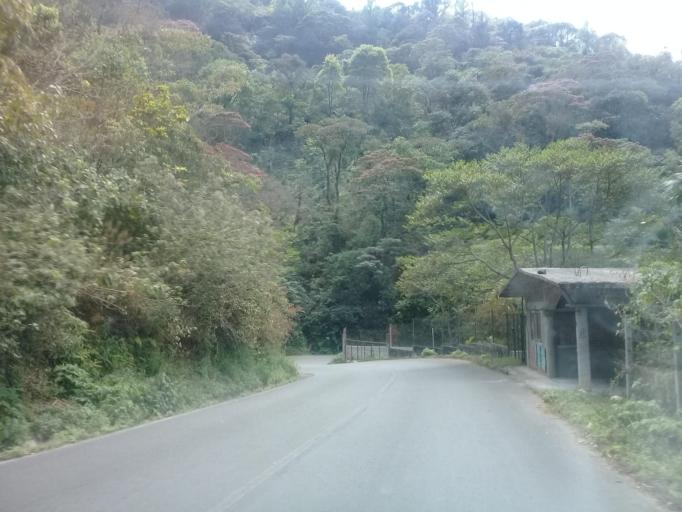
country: MX
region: Veracruz
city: Jalapilla
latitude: 18.8138
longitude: -97.0595
